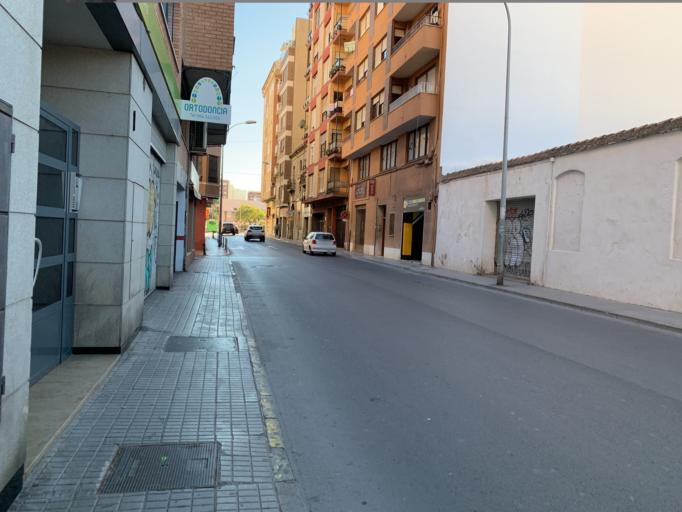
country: ES
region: Valencia
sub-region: Provincia de Castello
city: Castello de la Plana
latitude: 39.9859
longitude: -0.0444
